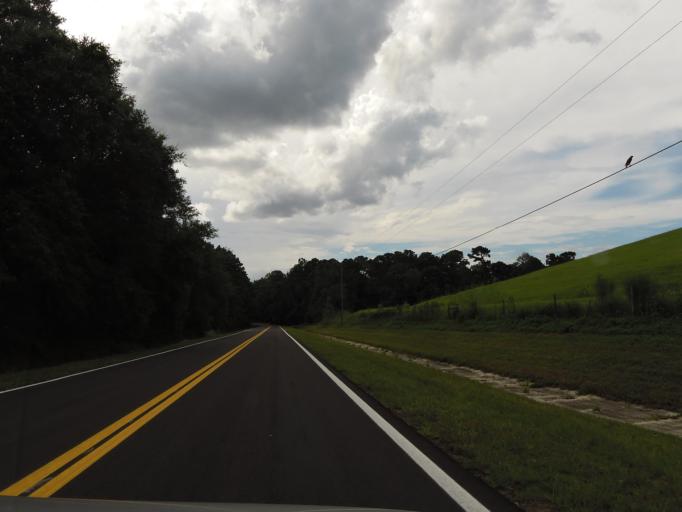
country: US
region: Florida
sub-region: Clay County
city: Green Cove Springs
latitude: 30.0058
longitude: -81.7459
